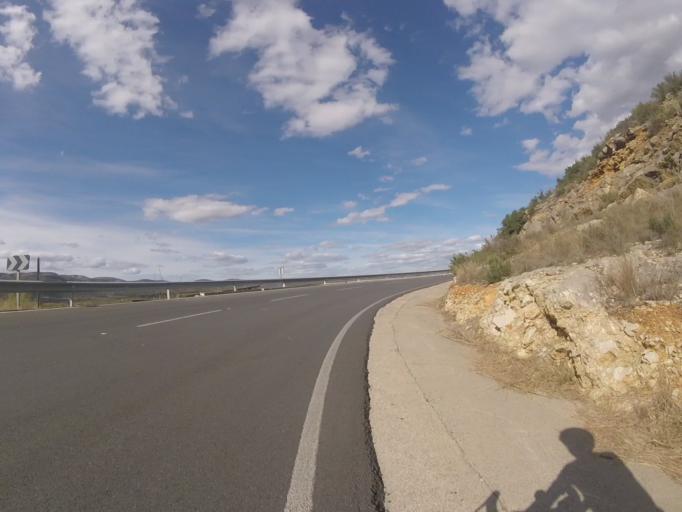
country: ES
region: Valencia
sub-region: Provincia de Castello
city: Cuevas de Vinroma
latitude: 40.3178
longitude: 0.1304
